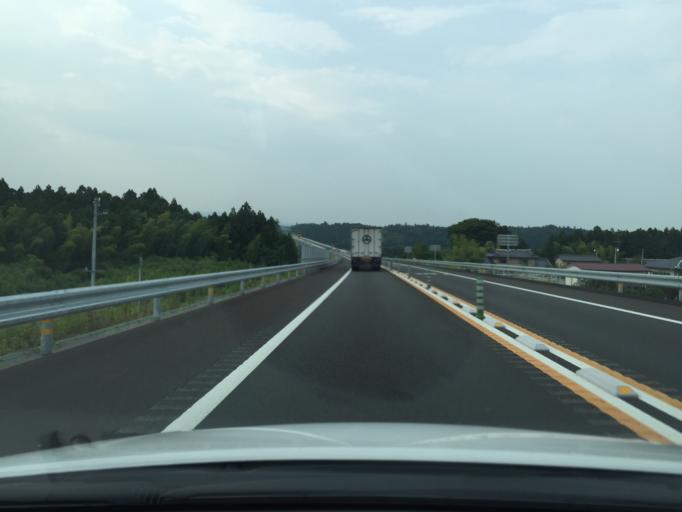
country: JP
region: Fukushima
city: Namie
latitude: 37.4709
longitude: 140.9618
